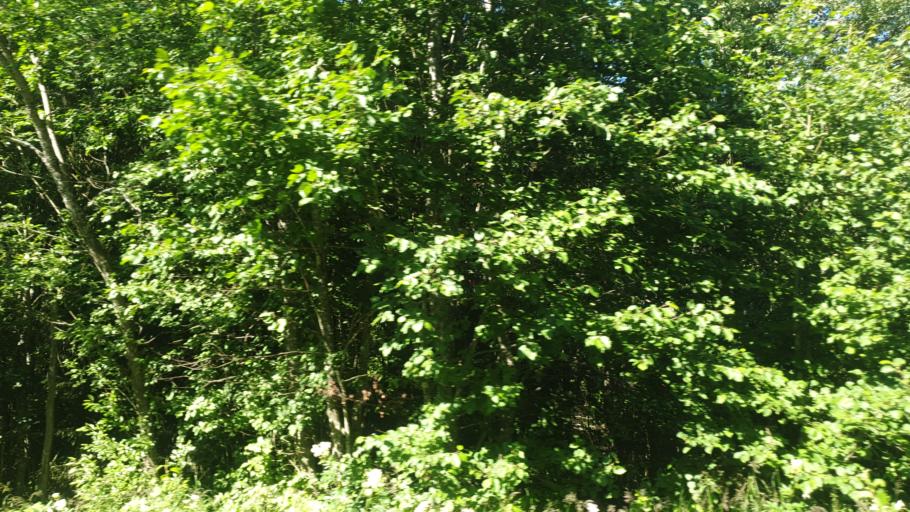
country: NO
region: Sor-Trondelag
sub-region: Meldal
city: Meldal
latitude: 63.1422
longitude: 9.7121
